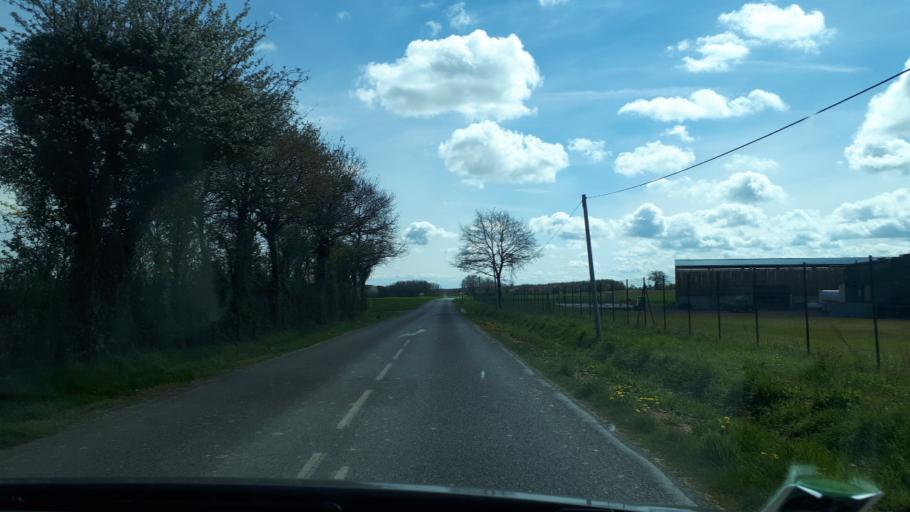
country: FR
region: Centre
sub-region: Departement du Loir-et-Cher
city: Lunay
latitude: 47.8611
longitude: 0.8812
